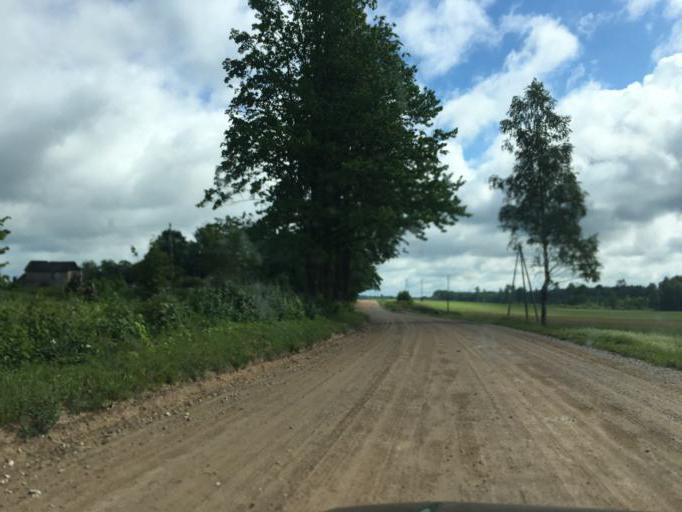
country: LV
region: Balvu Rajons
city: Balvi
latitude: 57.3297
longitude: 27.3216
